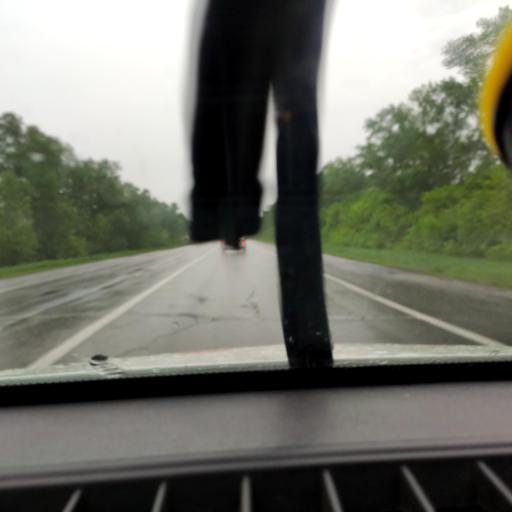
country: RU
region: Samara
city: Tol'yatti
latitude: 53.5996
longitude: 49.4087
